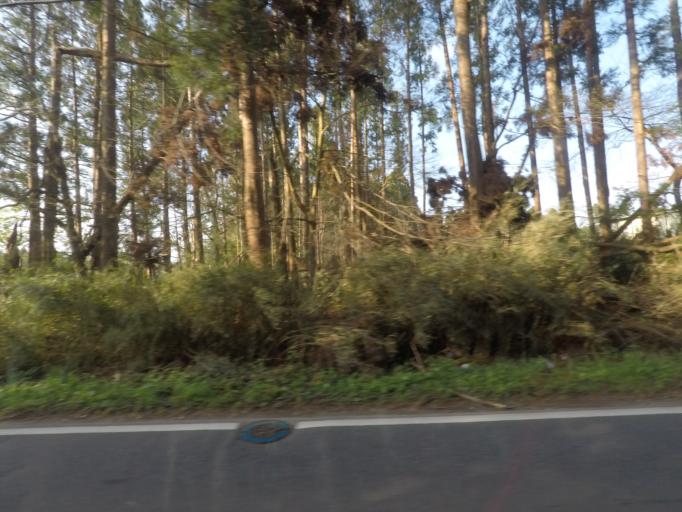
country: JP
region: Chiba
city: Yachimata
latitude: 35.6220
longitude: 140.2486
